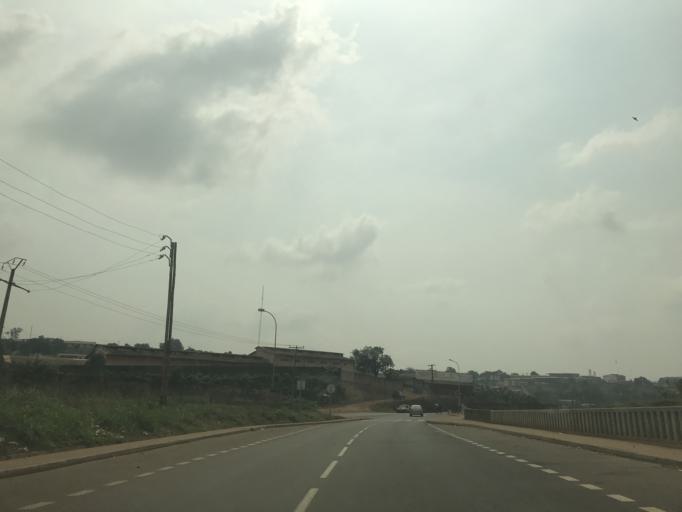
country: CM
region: Centre
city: Yaounde
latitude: 3.8345
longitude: 11.5144
